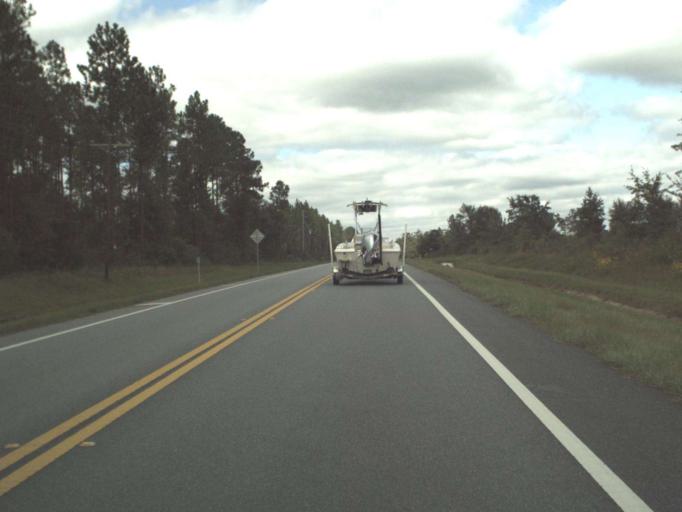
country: US
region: Florida
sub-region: Calhoun County
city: Blountstown
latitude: 30.3624
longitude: -85.2130
